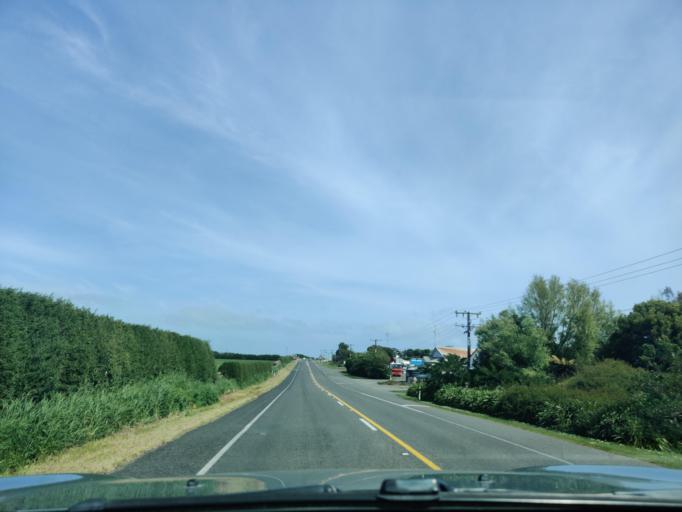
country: NZ
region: Taranaki
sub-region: South Taranaki District
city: Patea
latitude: -39.7131
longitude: 174.4486
